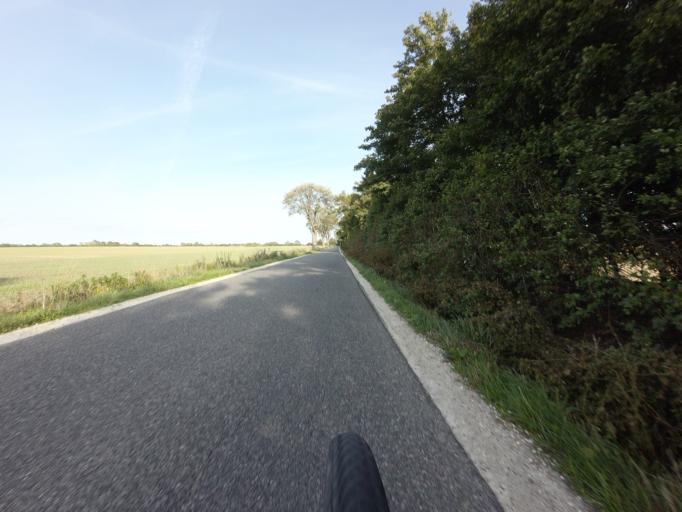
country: DK
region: Zealand
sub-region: Faxe Kommune
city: Fakse Ladeplads
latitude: 55.2523
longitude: 12.2430
